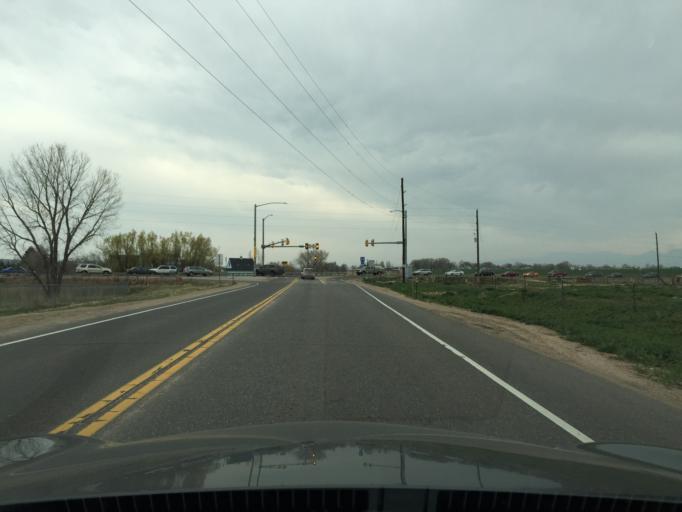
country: US
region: Colorado
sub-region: Boulder County
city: Lafayette
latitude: 40.0012
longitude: -105.0599
